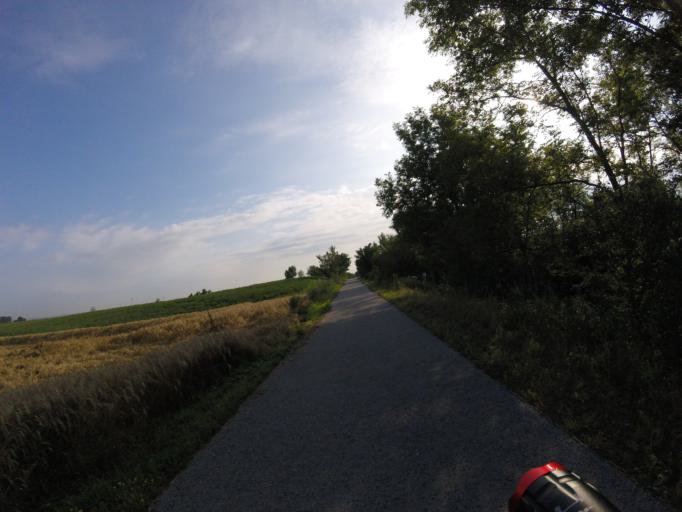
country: AT
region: Lower Austria
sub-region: Politischer Bezirk Baden
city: Trumau
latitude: 48.0078
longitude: 16.3584
